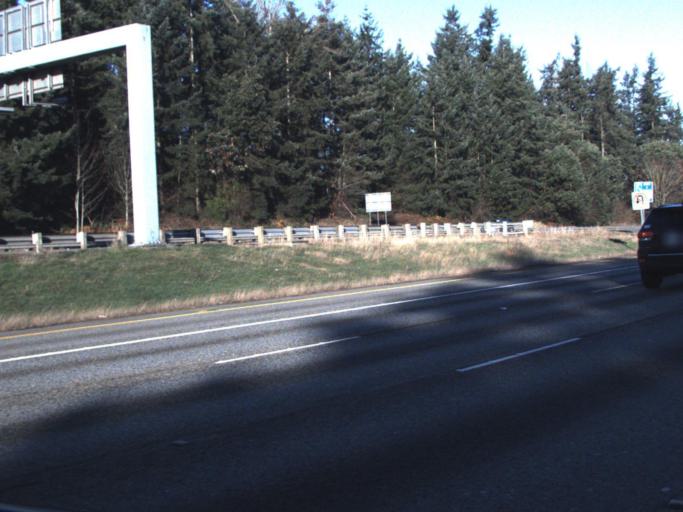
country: US
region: Washington
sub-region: King County
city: Lakeland North
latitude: 47.3348
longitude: -122.2933
